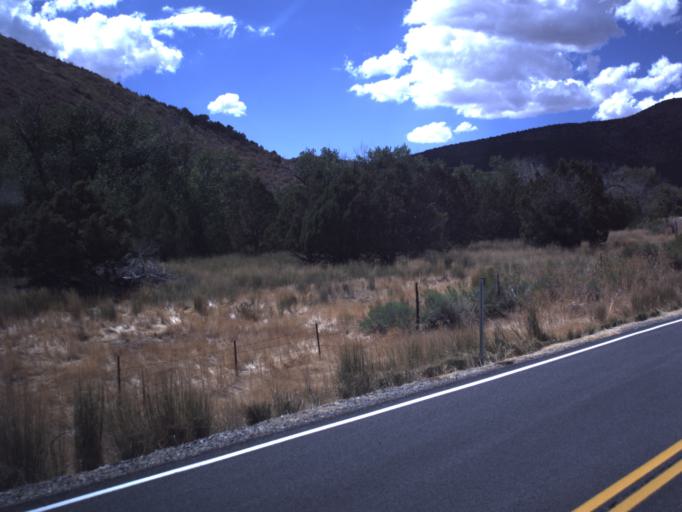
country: US
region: Utah
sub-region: Tooele County
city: Grantsville
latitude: 40.3424
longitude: -112.5418
